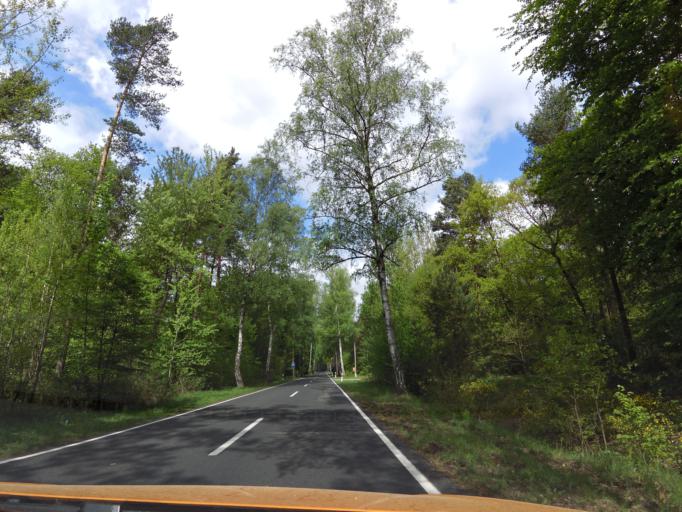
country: DE
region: Brandenburg
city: Gorzke
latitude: 52.0750
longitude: 12.2804
